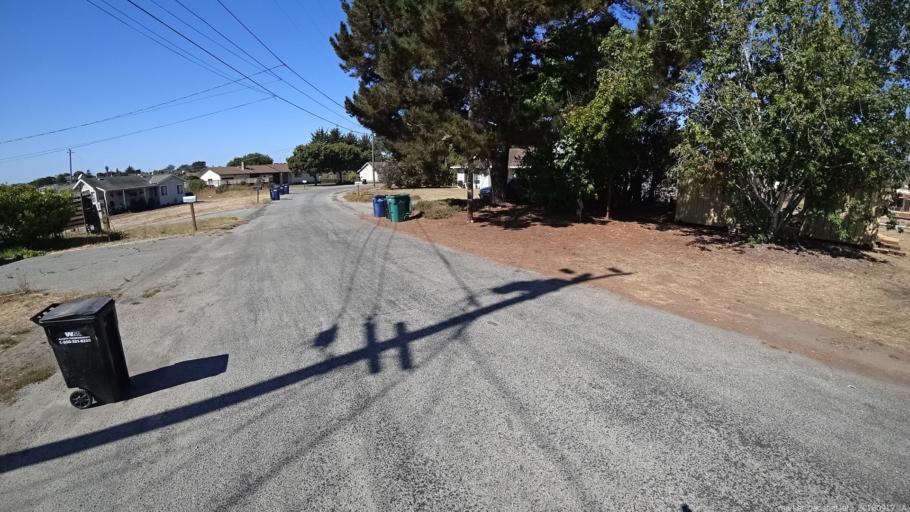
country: US
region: California
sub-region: Monterey County
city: Las Lomas
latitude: 36.8644
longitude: -121.7472
